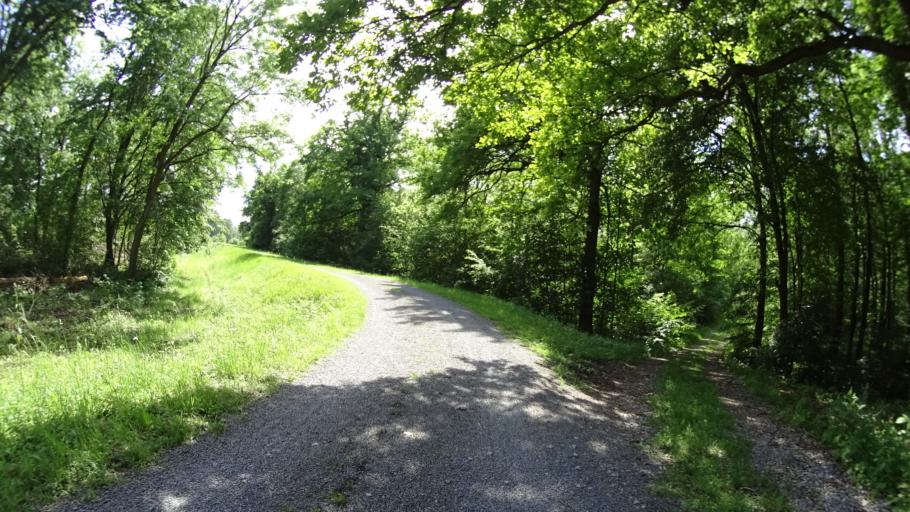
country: DE
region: Baden-Wuerttemberg
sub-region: Karlsruhe Region
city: Rheinstetten
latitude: 49.0228
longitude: 8.3213
